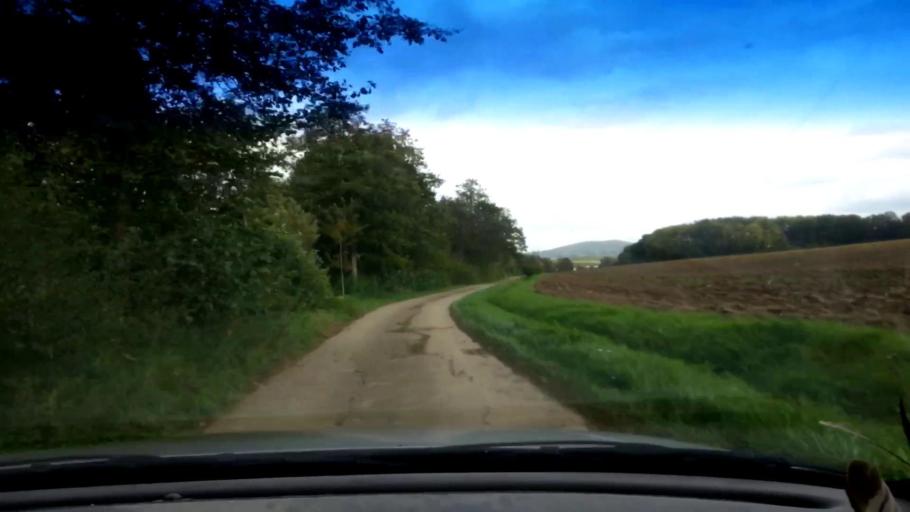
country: DE
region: Bavaria
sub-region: Upper Franconia
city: Schesslitz
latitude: 49.9958
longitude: 10.9830
